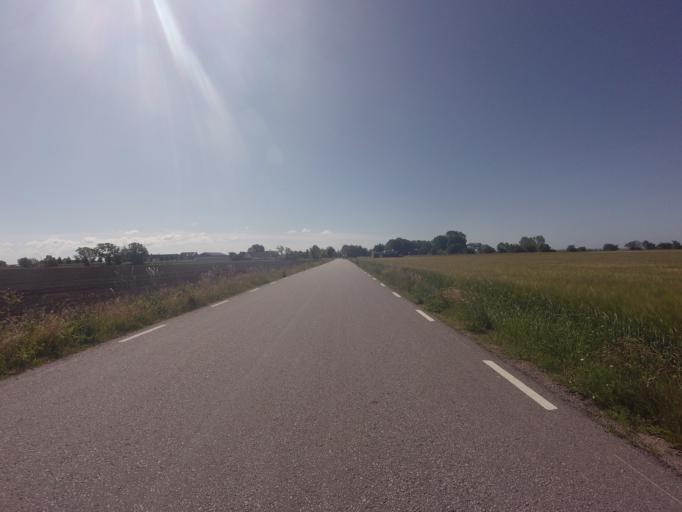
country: SE
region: Skane
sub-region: Malmo
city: Bunkeflostrand
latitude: 55.5126
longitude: 12.9366
